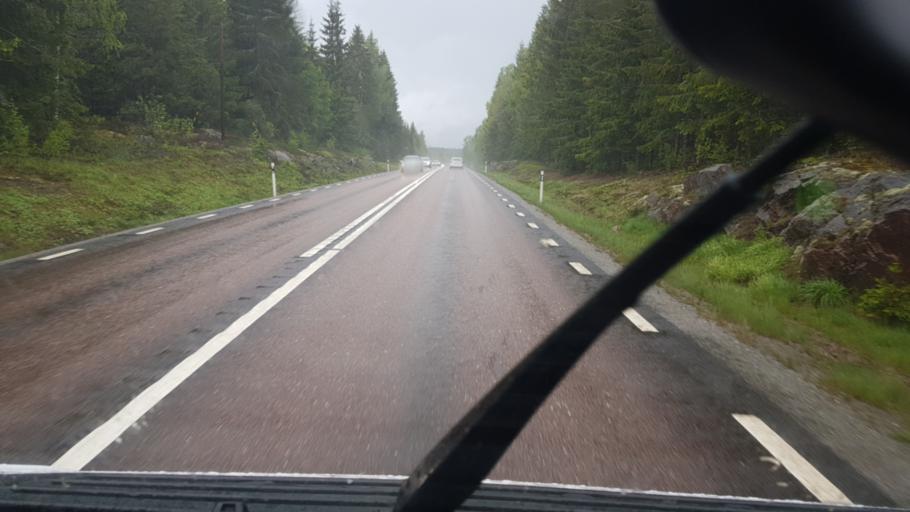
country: SE
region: Vaermland
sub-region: Sunne Kommun
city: Sunne
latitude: 59.6386
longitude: 12.9460
